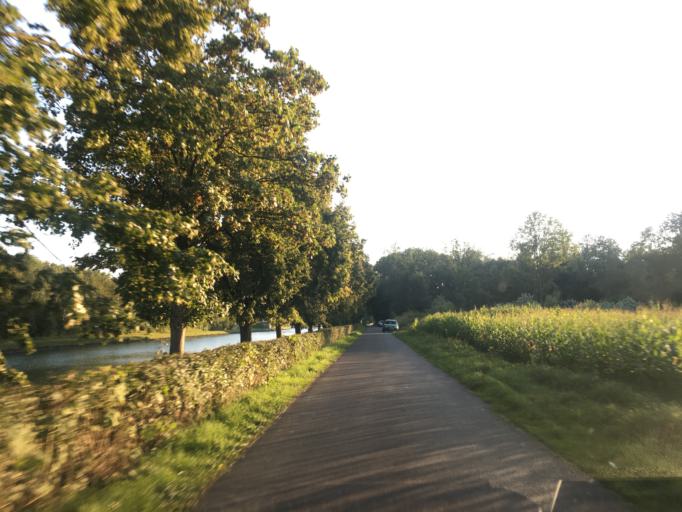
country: DE
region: North Rhine-Westphalia
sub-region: Regierungsbezirk Munster
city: Muenster
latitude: 51.8851
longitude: 7.5879
